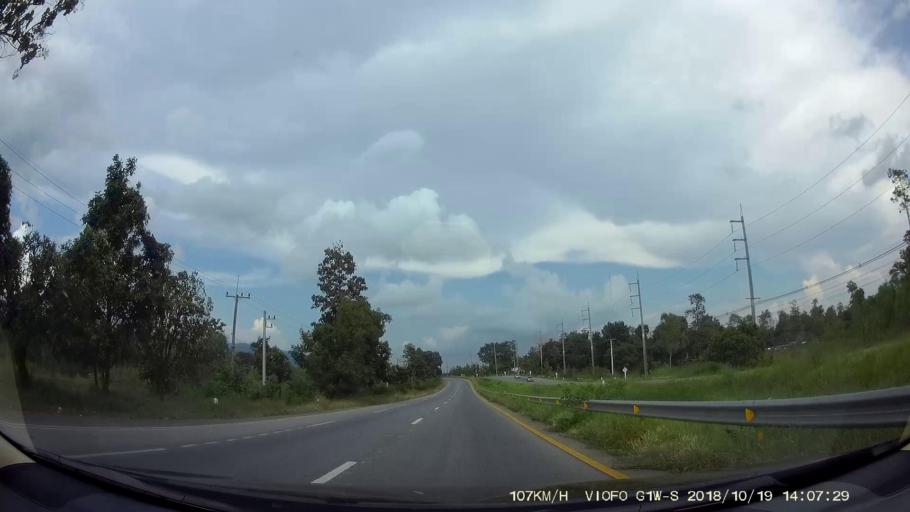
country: TH
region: Chaiyaphum
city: Chaiyaphum
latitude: 15.8945
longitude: 102.1175
